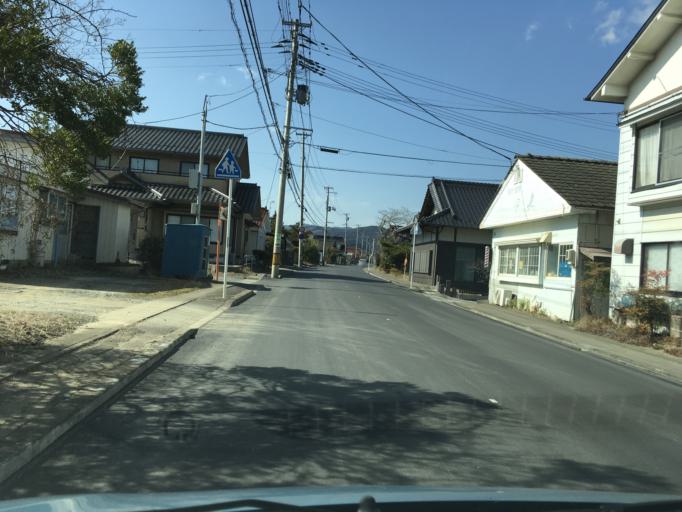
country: JP
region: Iwate
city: Ofunato
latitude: 38.8320
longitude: 141.5853
